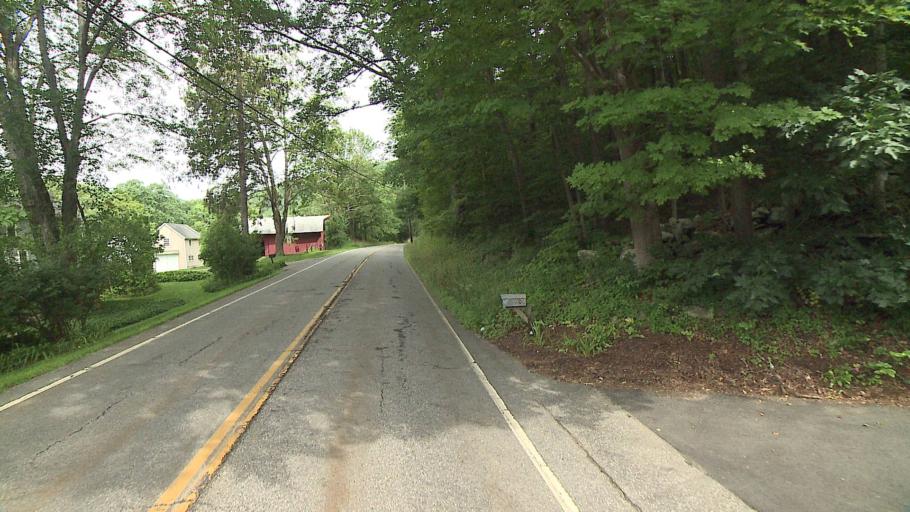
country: US
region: Connecticut
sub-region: Litchfield County
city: Kent
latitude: 41.7491
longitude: -73.5077
